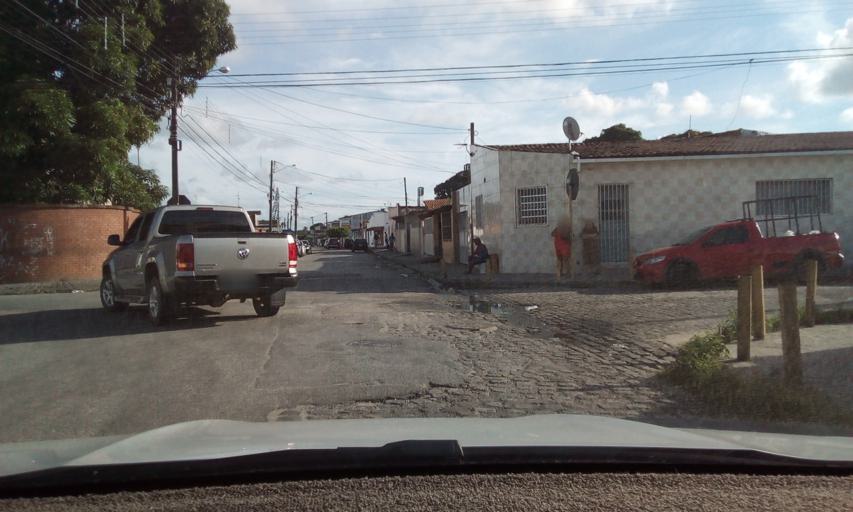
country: BR
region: Paraiba
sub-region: Joao Pessoa
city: Joao Pessoa
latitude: -7.1388
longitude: -34.8892
